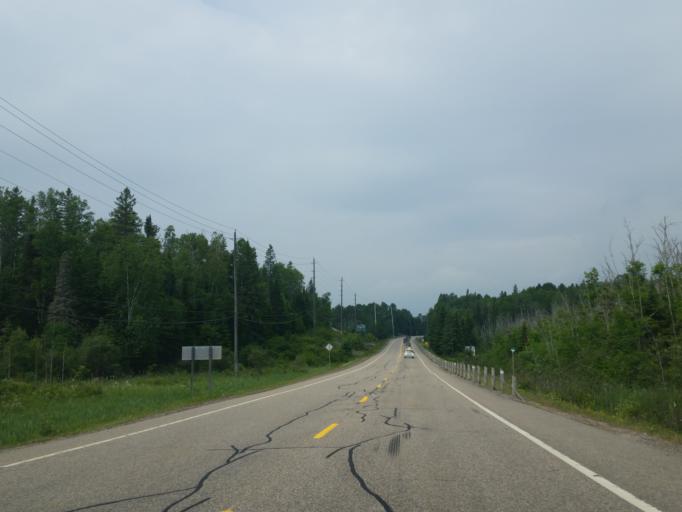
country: CA
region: Ontario
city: Bancroft
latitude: 45.4896
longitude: -78.2222
